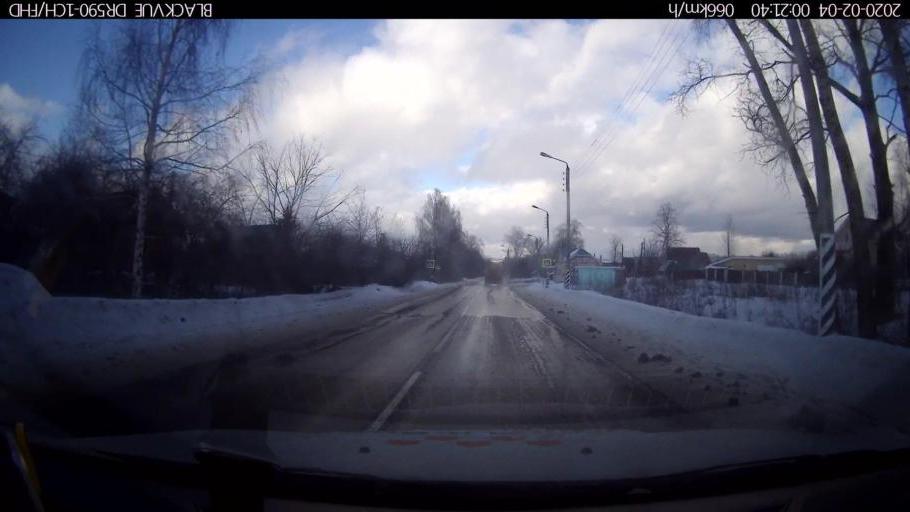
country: RU
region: Nizjnij Novgorod
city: Kstovo
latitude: 55.9642
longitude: 44.2097
